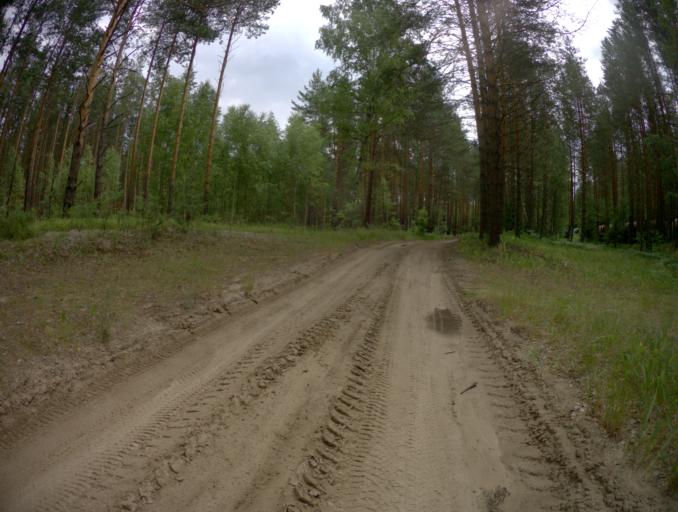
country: RU
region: Nizjnij Novgorod
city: Frolishchi
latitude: 56.3158
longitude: 42.6508
